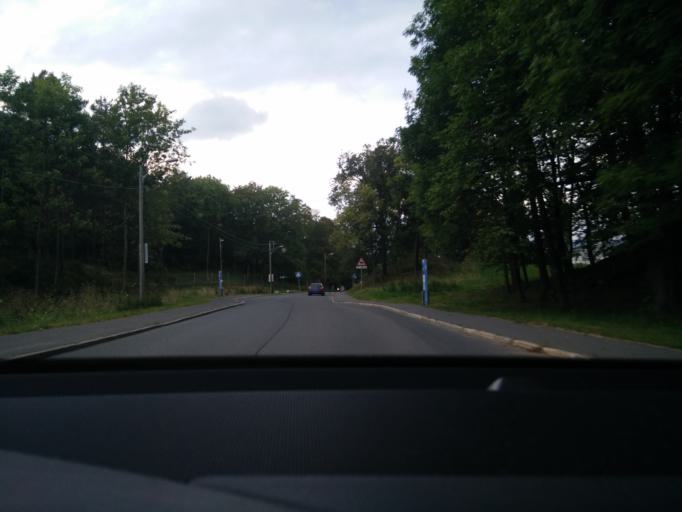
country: NO
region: Oslo
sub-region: Oslo
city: Sjolyststranda
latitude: 59.9089
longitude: 10.6815
